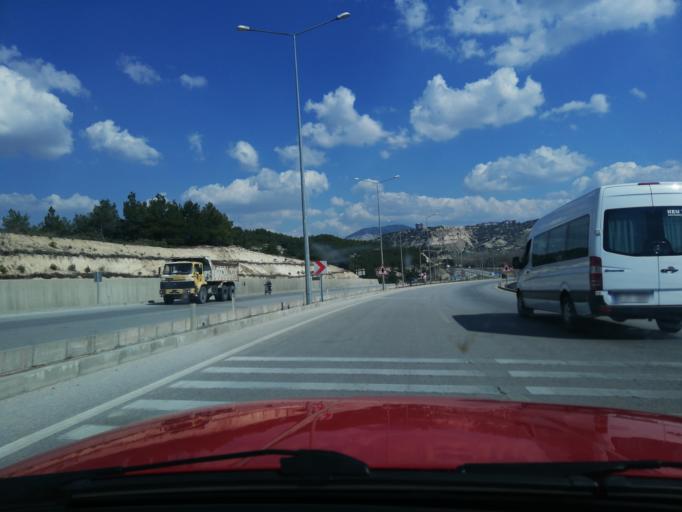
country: TR
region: Burdur
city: Burdur
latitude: 37.7008
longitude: 30.3171
